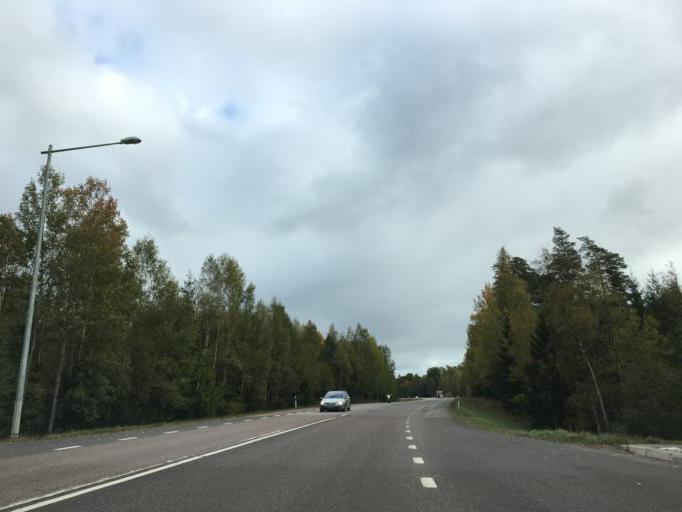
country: SE
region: Soedermanland
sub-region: Nykopings Kommun
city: Svalsta
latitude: 58.7710
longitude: 16.9307
